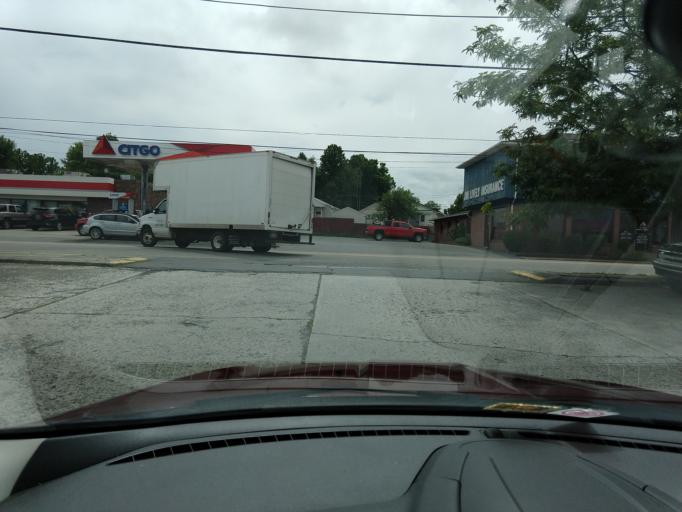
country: US
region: West Virginia
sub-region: Fayette County
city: Oak Hill
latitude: 37.9752
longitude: -81.1556
